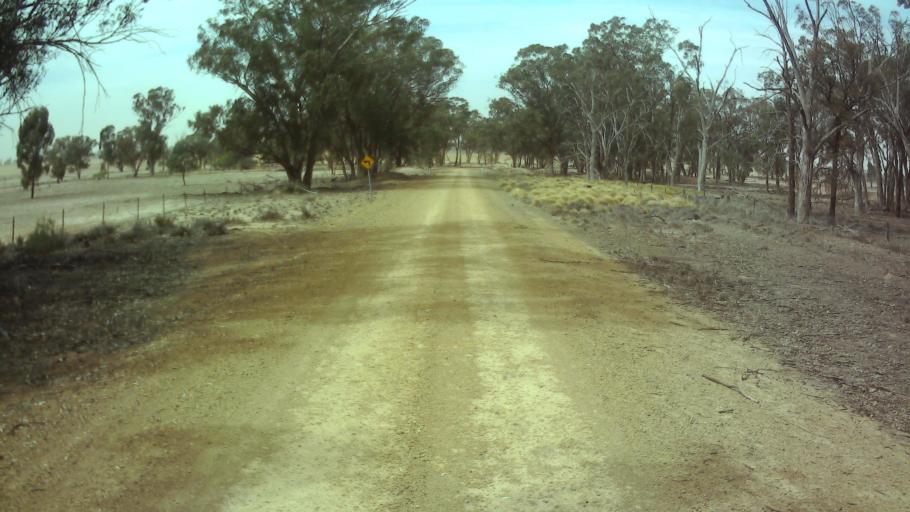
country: AU
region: New South Wales
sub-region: Weddin
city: Grenfell
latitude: -33.7413
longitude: 147.9608
